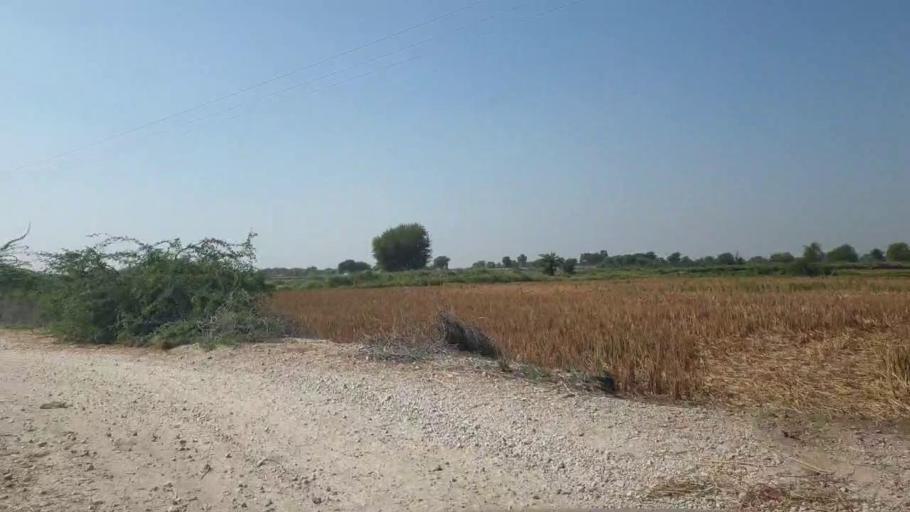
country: PK
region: Sindh
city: Talhar
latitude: 24.8349
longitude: 68.8004
